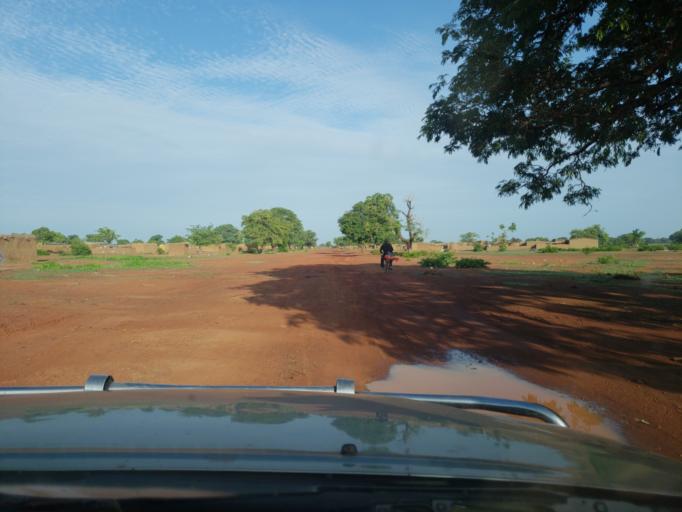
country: ML
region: Sikasso
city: Koutiala
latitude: 12.4295
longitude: -5.6118
